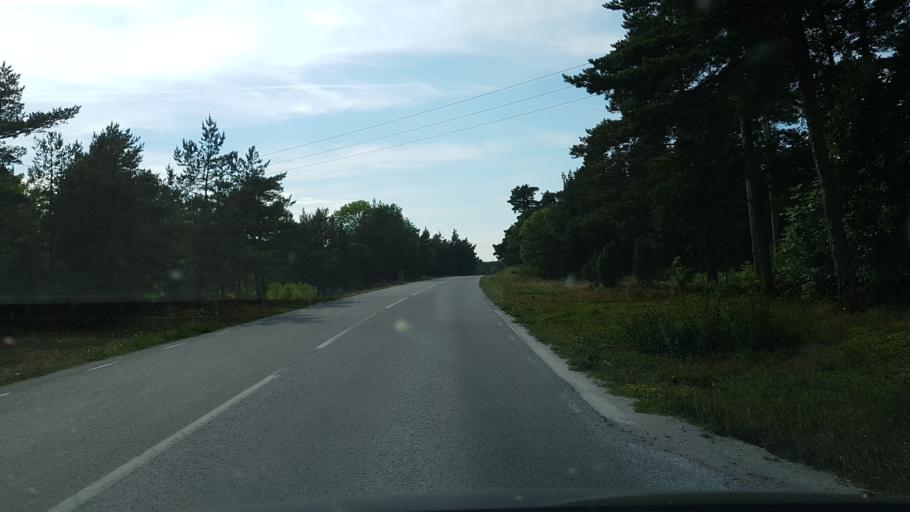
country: SE
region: Gotland
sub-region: Gotland
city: Visby
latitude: 57.6316
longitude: 18.4161
